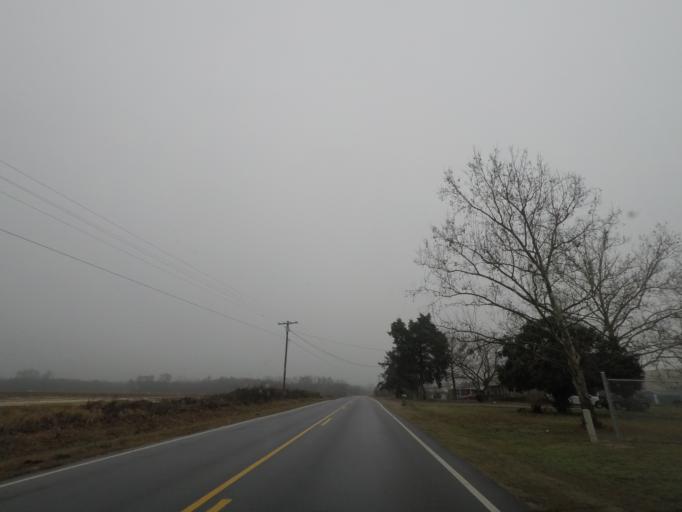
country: US
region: North Carolina
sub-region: Scotland County
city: Laurinburg
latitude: 34.8062
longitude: -79.4410
